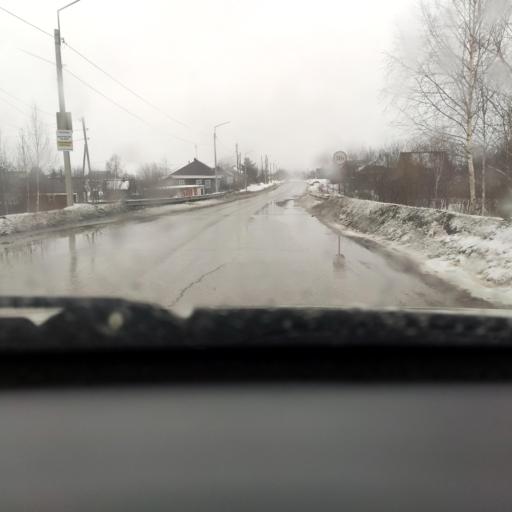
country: RU
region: Perm
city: Yugo-Kamskiy
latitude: 57.7037
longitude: 55.6082
